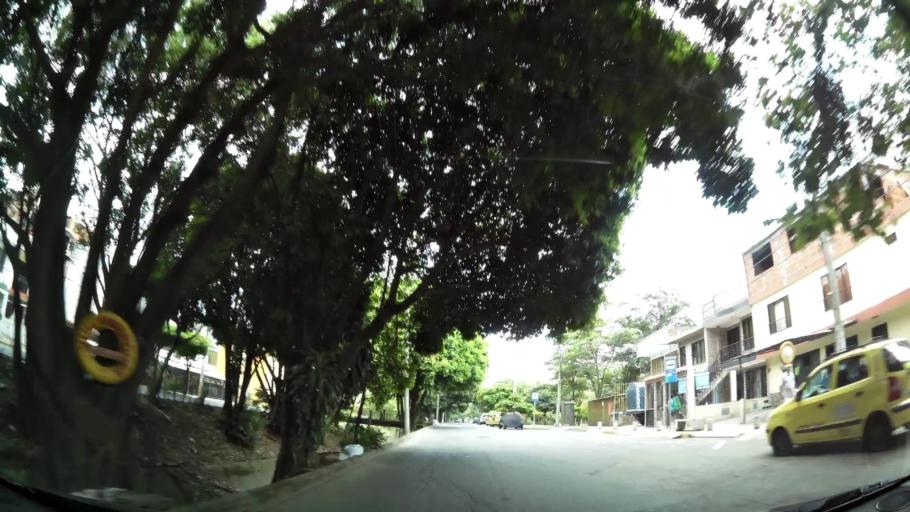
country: CO
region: Valle del Cauca
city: Cali
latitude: 3.4681
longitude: -76.4931
